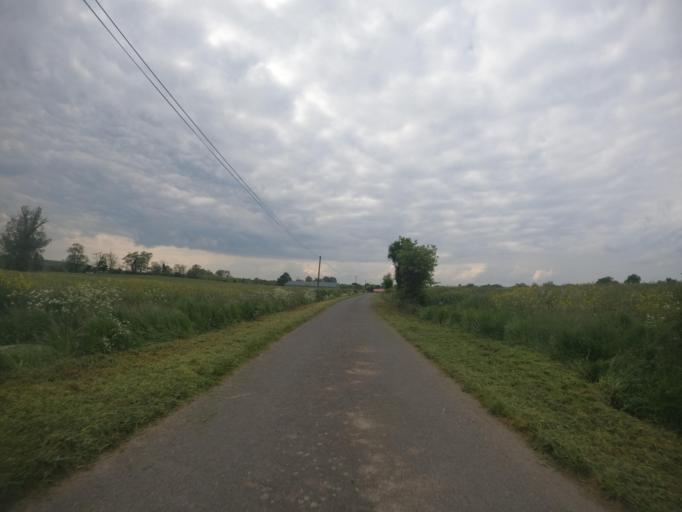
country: FR
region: Poitou-Charentes
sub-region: Departement des Deux-Sevres
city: Chiche
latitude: 46.8491
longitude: -0.3096
